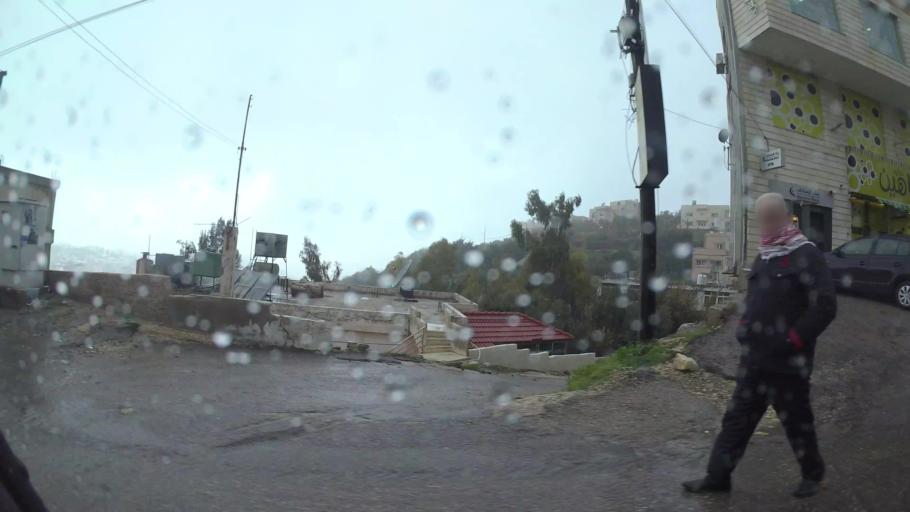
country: JO
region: Amman
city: Wadi as Sir
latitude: 32.0028
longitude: 35.7909
